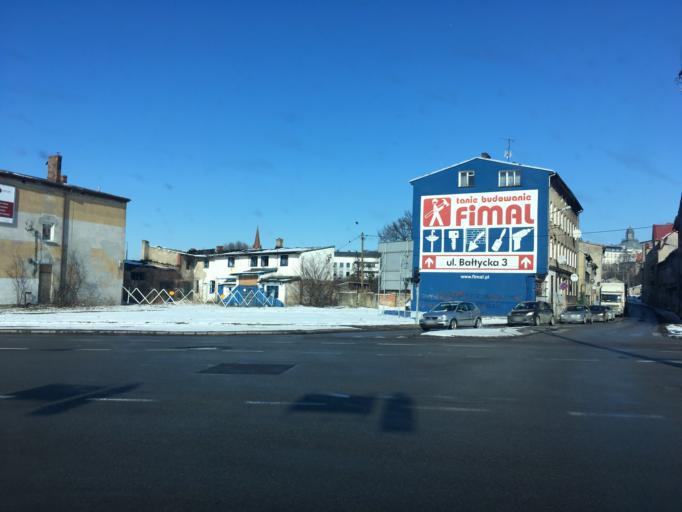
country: PL
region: Pomeranian Voivodeship
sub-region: Slupsk
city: Slupsk
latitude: 54.4648
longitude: 17.0414
